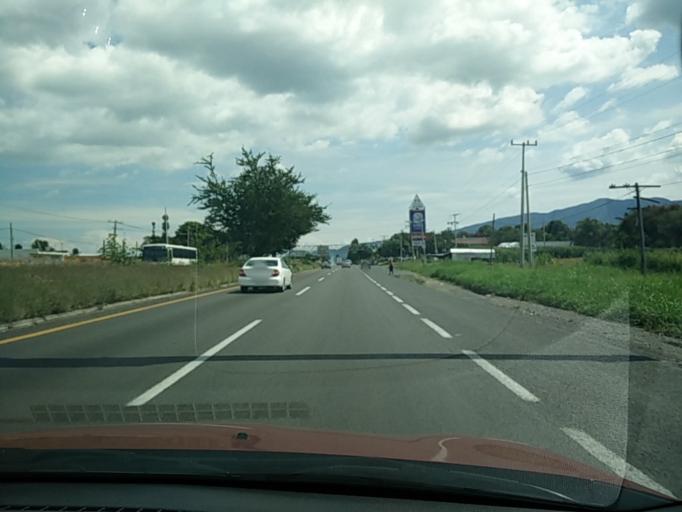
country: MX
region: Jalisco
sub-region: Ixtlahuacan de los Membrillos
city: Los Olivos
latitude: 20.4198
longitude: -103.2358
